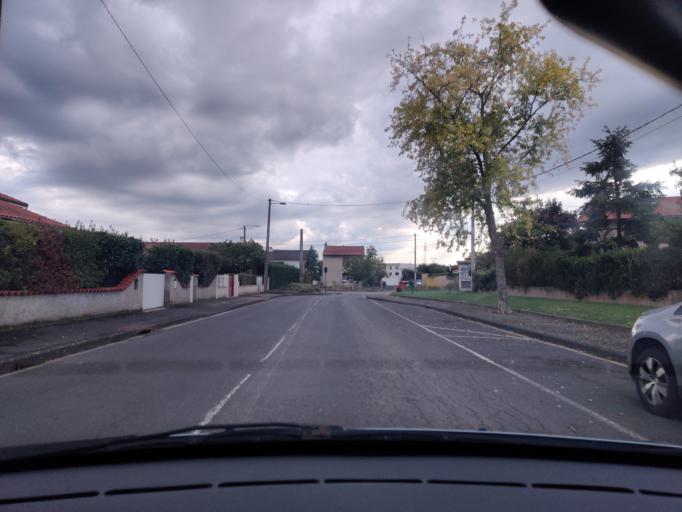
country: FR
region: Auvergne
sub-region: Departement du Puy-de-Dome
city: Menetrol
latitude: 45.8823
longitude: 3.1272
